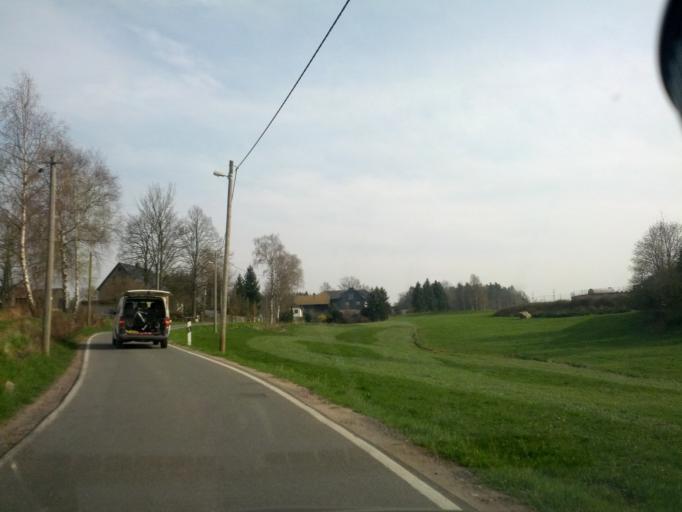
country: DE
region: Saxony
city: Kirchberg
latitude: 50.5839
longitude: 12.5131
